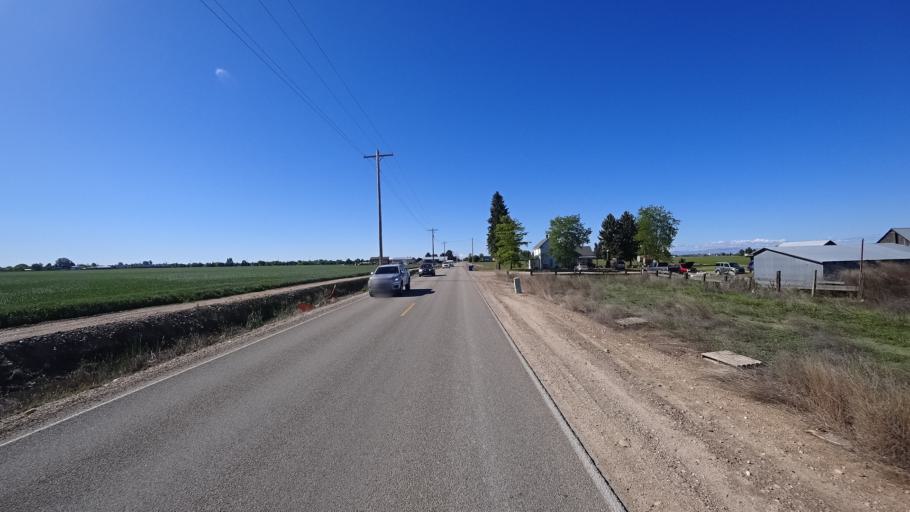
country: US
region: Idaho
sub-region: Ada County
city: Star
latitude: 43.6419
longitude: -116.4536
